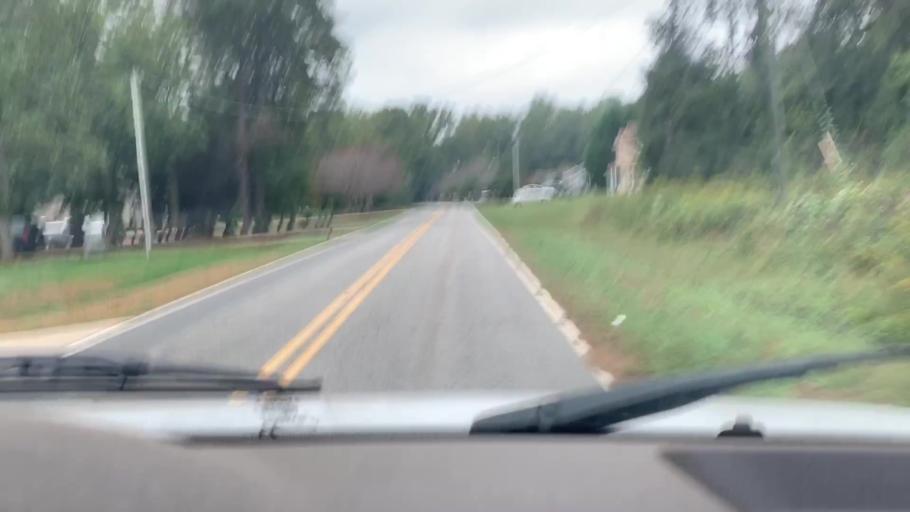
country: US
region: North Carolina
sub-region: Catawba County
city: Lake Norman of Catawba
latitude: 35.5589
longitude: -80.9004
